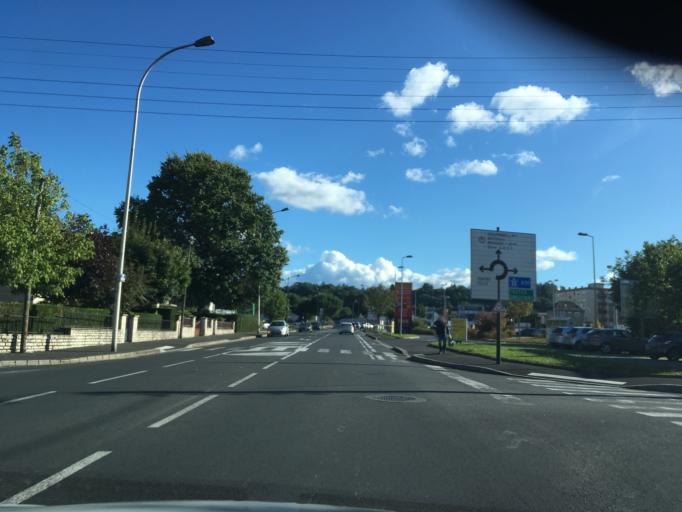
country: FR
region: Limousin
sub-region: Departement de la Correze
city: Brive-la-Gaillarde
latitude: 45.1540
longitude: 1.5046
